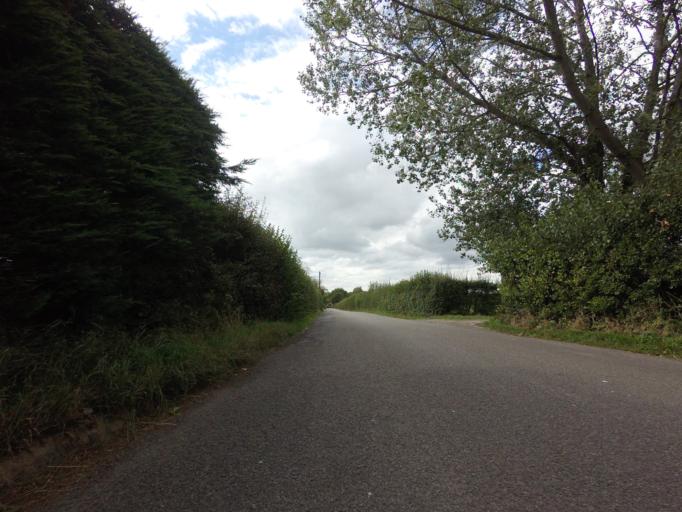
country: GB
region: England
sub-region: Kent
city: Marden
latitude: 51.1601
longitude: 0.4444
